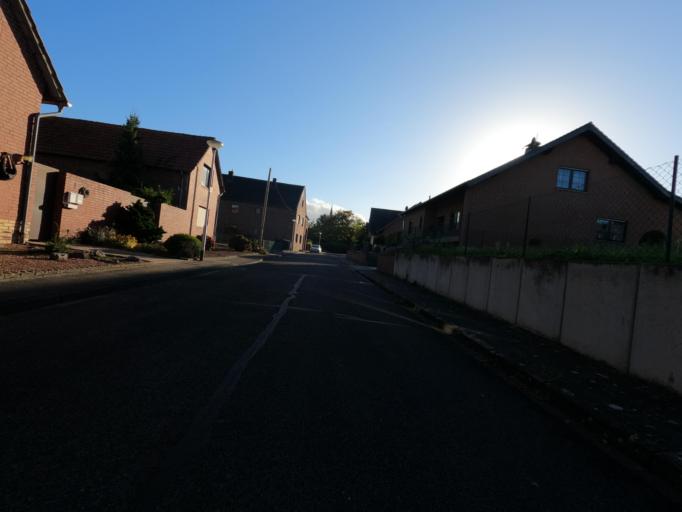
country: DE
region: North Rhine-Westphalia
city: Huckelhoven
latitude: 51.0297
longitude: 6.1766
